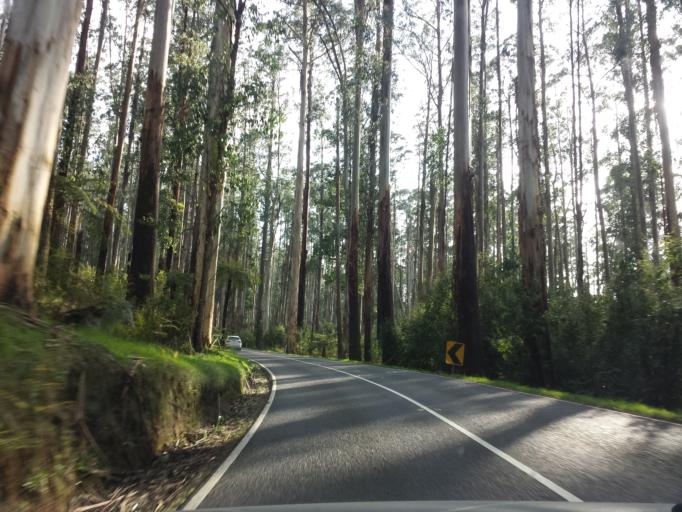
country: AU
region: Victoria
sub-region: Yarra Ranges
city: Healesville
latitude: -37.6130
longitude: 145.6056
